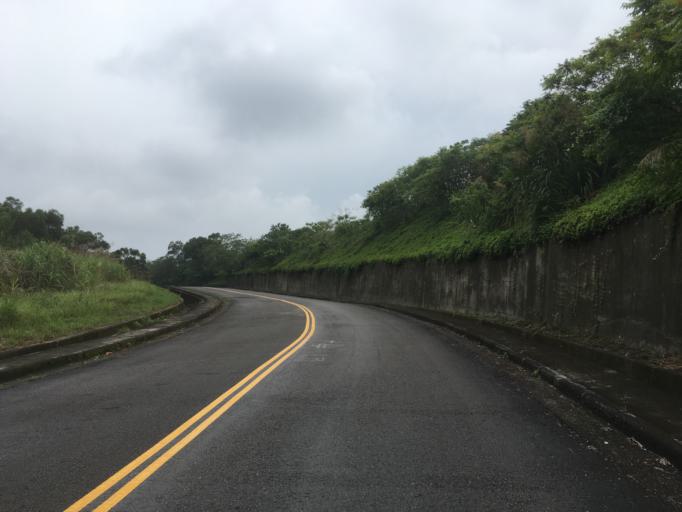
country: TW
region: Taiwan
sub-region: Taichung City
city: Taichung
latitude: 24.1670
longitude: 120.7723
